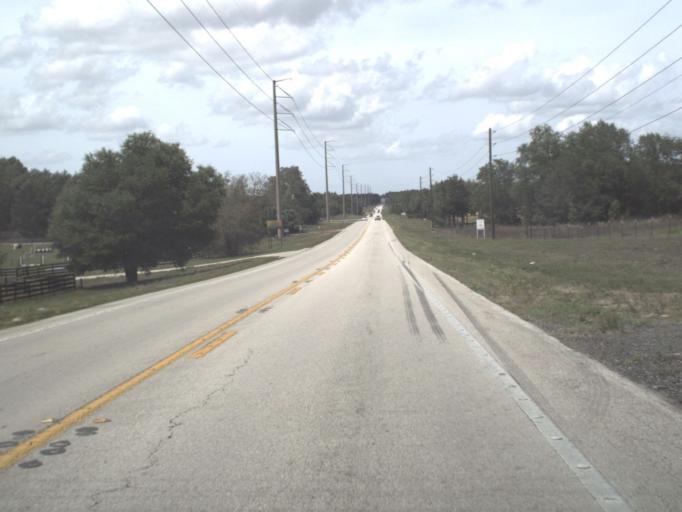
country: US
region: Florida
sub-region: Lake County
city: Mount Plymouth
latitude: 28.8513
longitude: -81.5850
